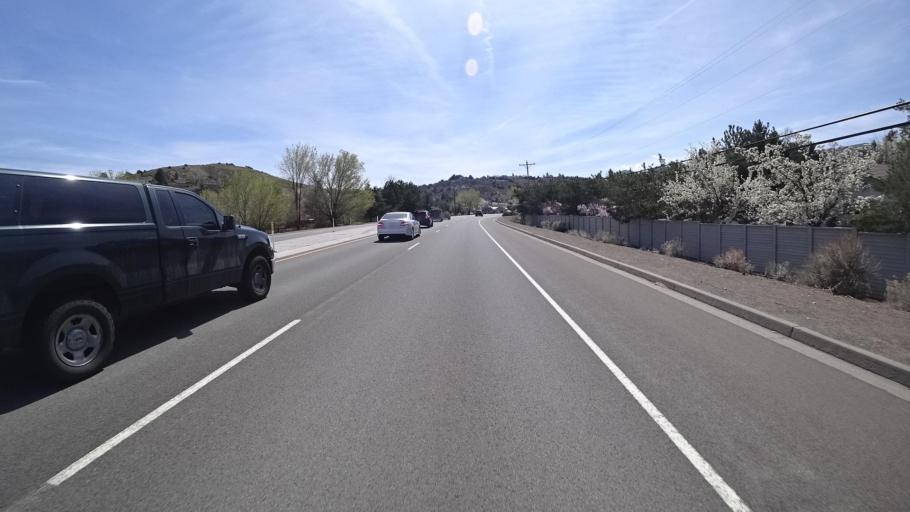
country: US
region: Nevada
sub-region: Washoe County
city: Reno
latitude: 39.5027
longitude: -119.8585
